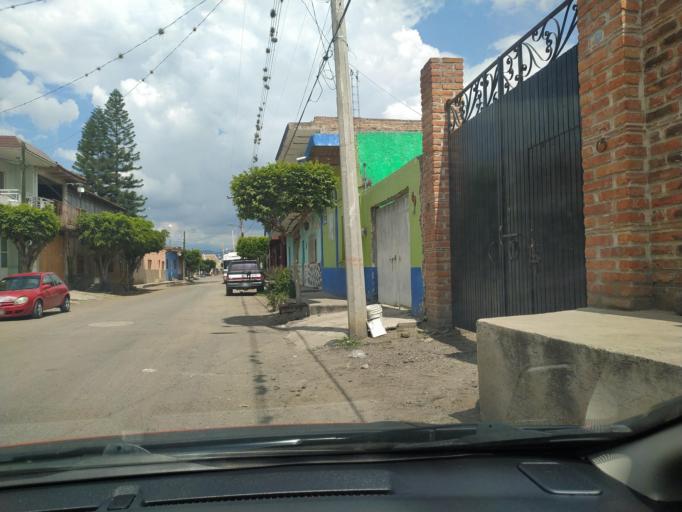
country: MX
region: Jalisco
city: Villa Corona
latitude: 20.3515
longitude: -103.6746
